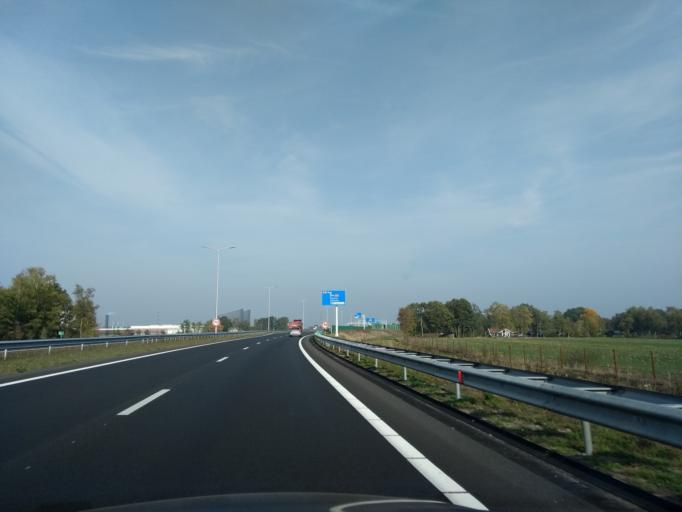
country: NL
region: Overijssel
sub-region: Gemeente Hengelo
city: Hengelo
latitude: 52.2007
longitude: 6.8193
